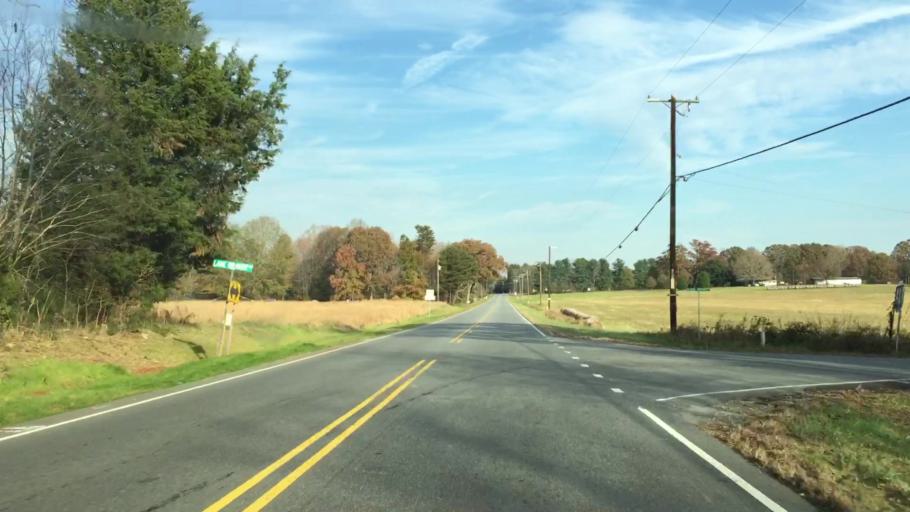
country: US
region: North Carolina
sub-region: Guilford County
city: Summerfield
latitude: 36.2560
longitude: -79.8838
